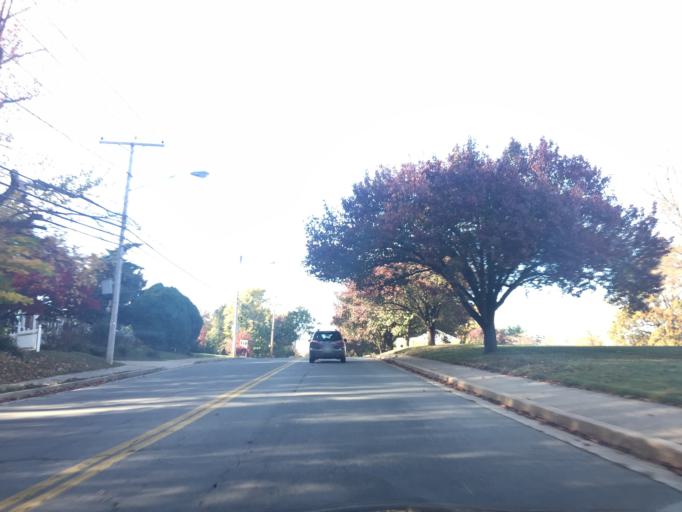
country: US
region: Maryland
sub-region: Baltimore County
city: Parkville
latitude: 39.3678
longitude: -76.5362
